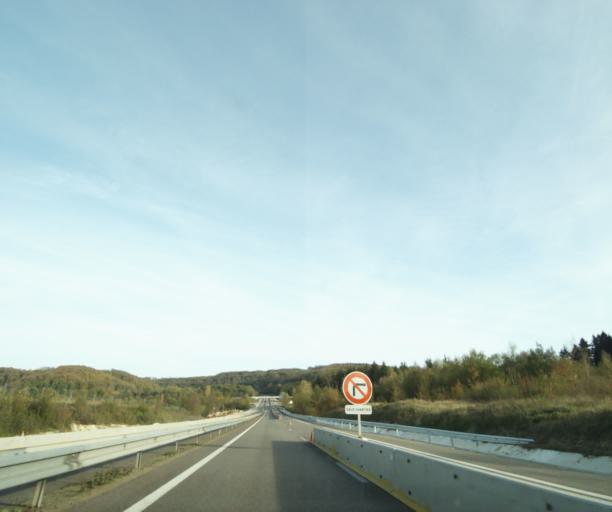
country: FR
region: Lorraine
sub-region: Departement de la Meuse
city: Clermont-en-Argonne
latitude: 49.0922
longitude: 4.9921
